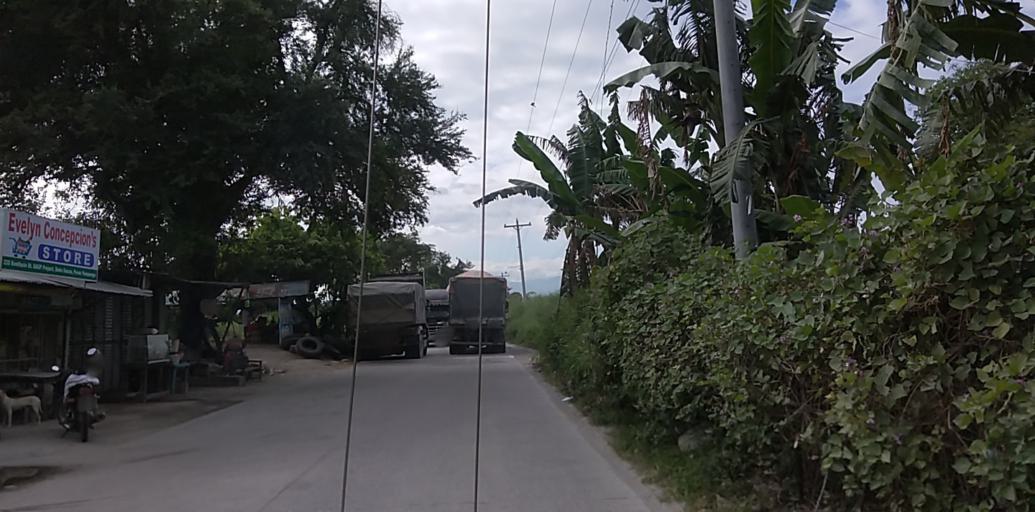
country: PH
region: Central Luzon
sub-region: Province of Pampanga
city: Porac
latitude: 15.0688
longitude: 120.5551
